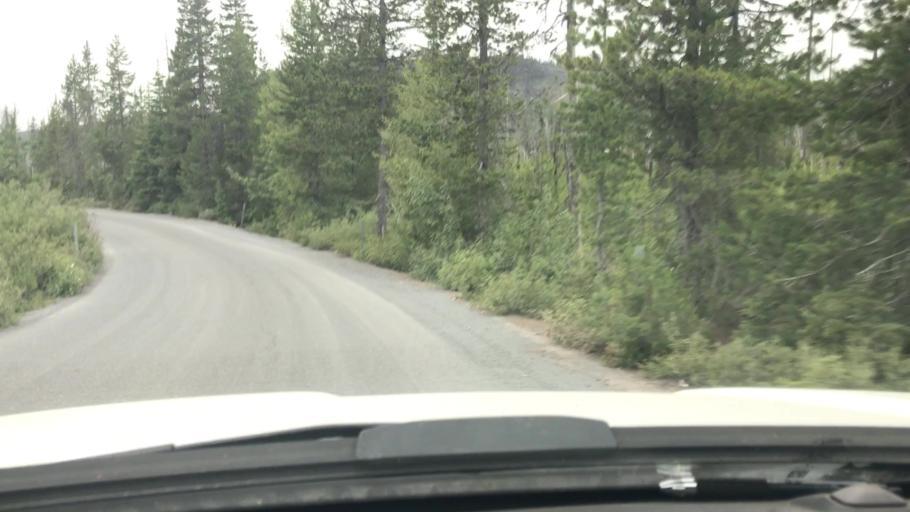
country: US
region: Oregon
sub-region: Deschutes County
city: Sisters
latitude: 44.4199
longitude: -121.8596
